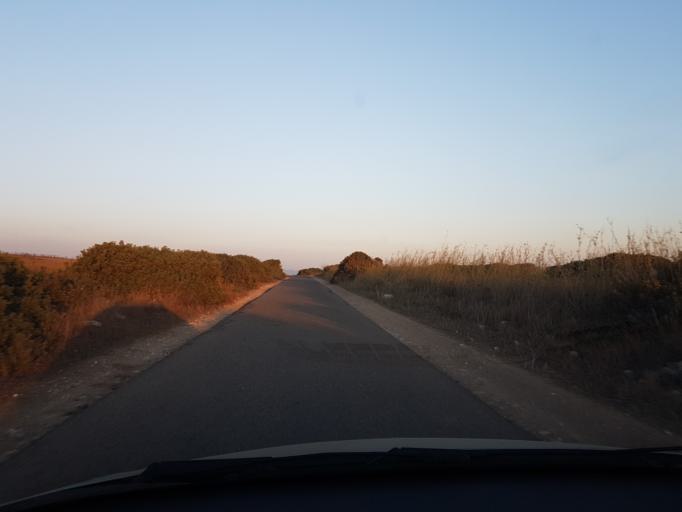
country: IT
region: Sardinia
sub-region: Provincia di Oristano
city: Cabras
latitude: 39.9663
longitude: 8.4317
